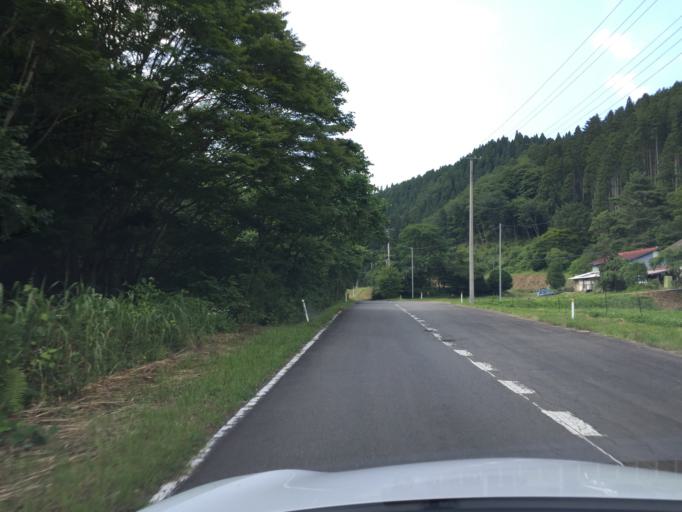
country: JP
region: Fukushima
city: Ishikawa
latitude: 37.1117
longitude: 140.6570
